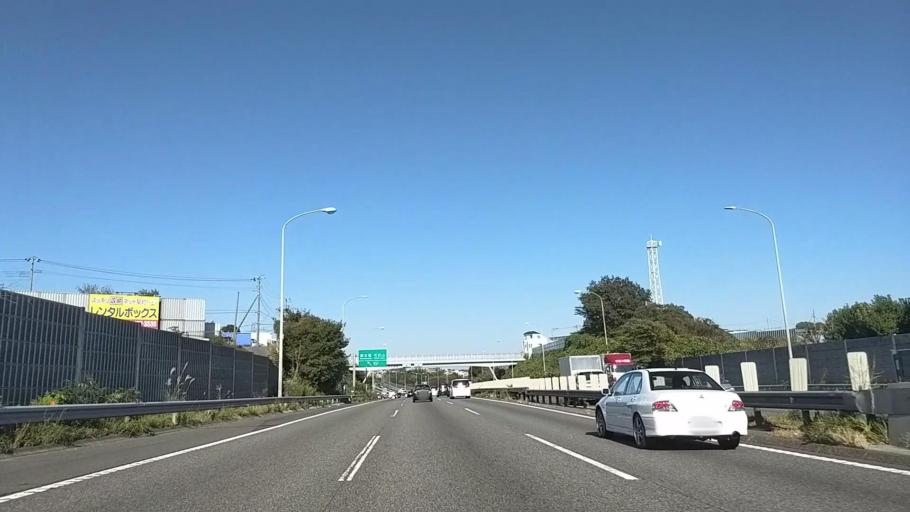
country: JP
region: Kanagawa
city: Yokohama
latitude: 35.4592
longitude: 139.5458
